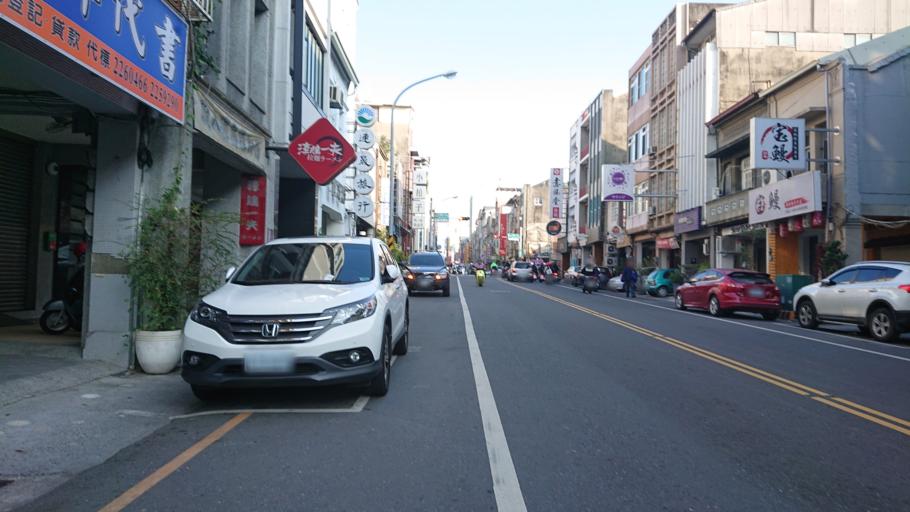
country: TW
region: Taiwan
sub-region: Tainan
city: Tainan
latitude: 22.9957
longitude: 120.2011
